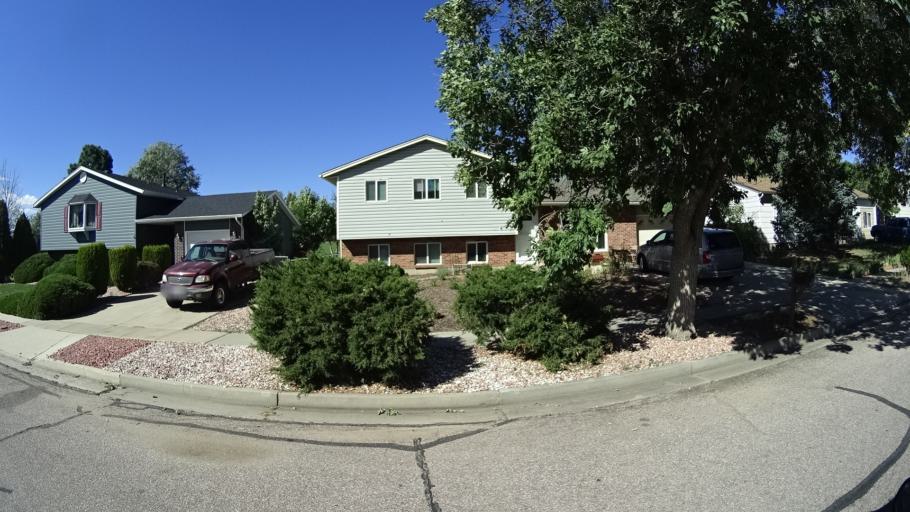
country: US
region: Colorado
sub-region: El Paso County
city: Stratmoor
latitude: 38.7908
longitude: -104.7521
